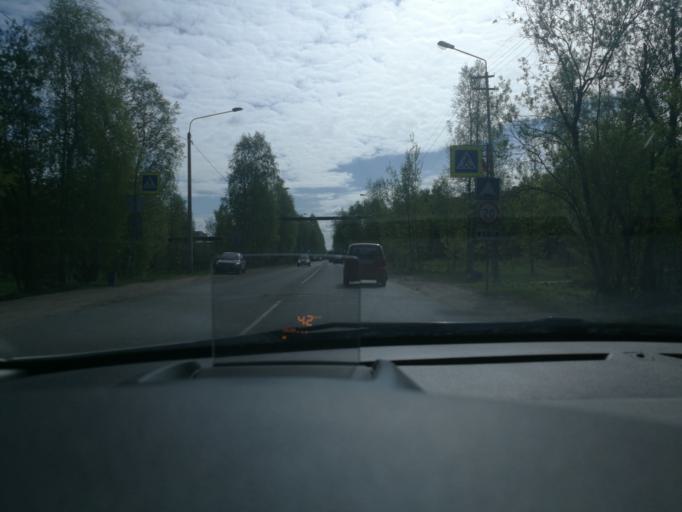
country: RU
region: Arkhangelskaya
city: Arkhangel'sk
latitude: 64.5931
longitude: 40.5866
